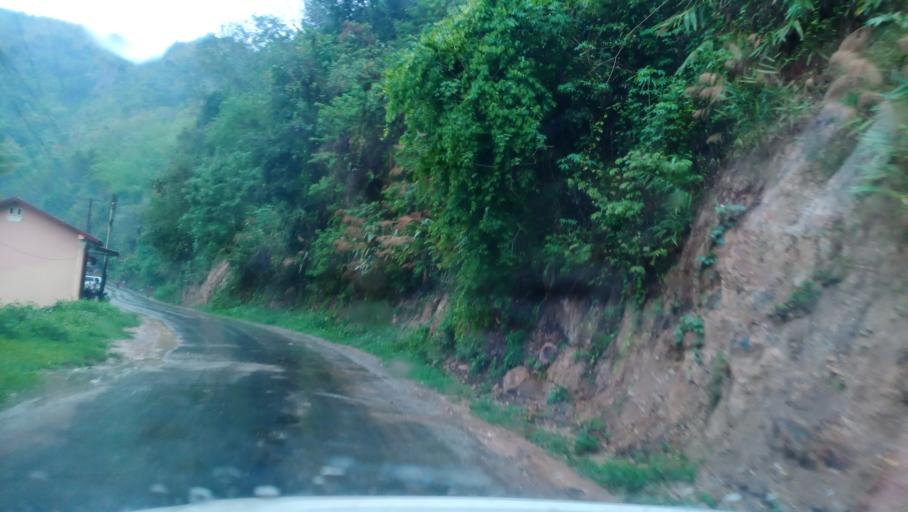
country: LA
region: Phongsali
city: Khoa
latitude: 21.0806
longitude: 102.5041
